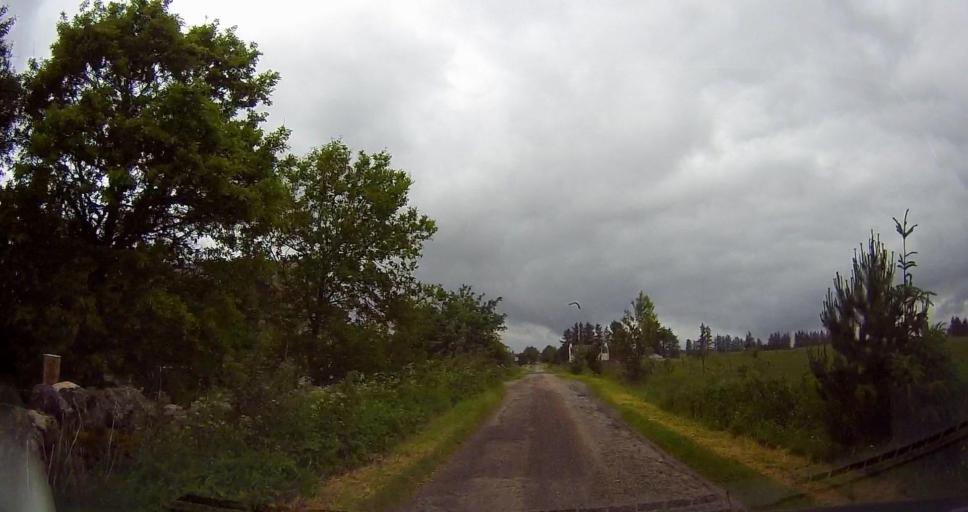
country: GB
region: Scotland
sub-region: Highland
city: Alness
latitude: 58.0727
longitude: -4.4363
